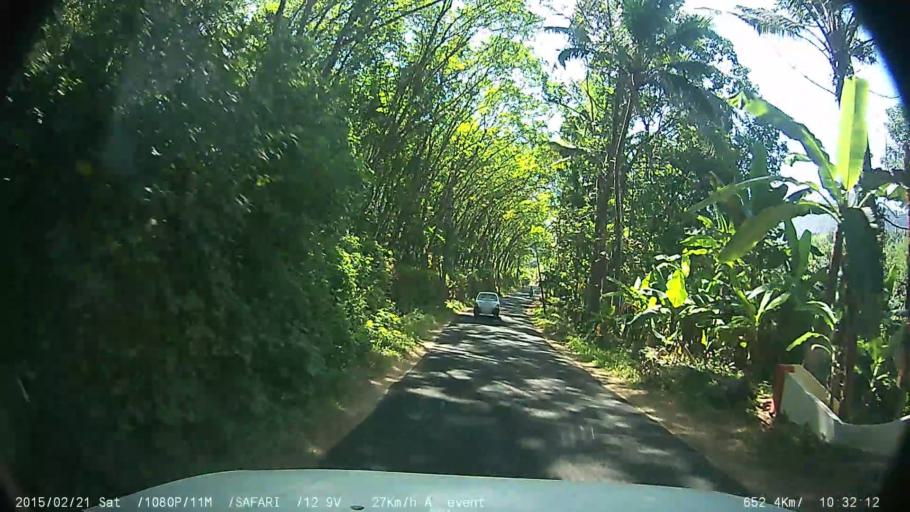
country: IN
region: Kerala
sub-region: Kottayam
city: Lalam
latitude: 9.8408
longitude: 76.7094
